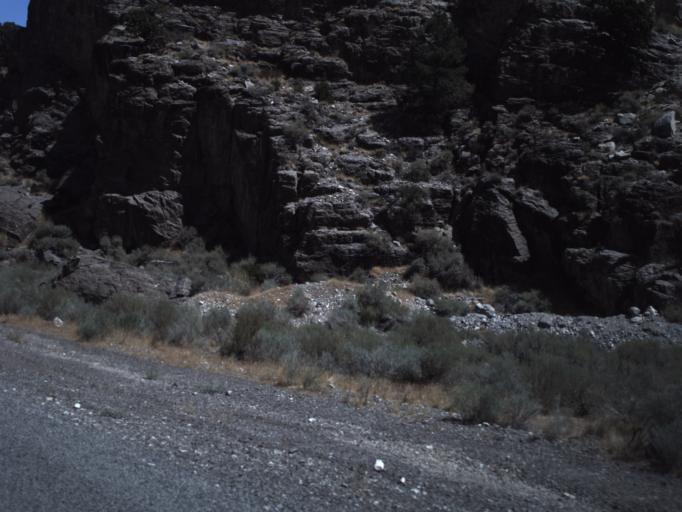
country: US
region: Utah
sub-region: Beaver County
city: Milford
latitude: 39.0851
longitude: -113.5694
